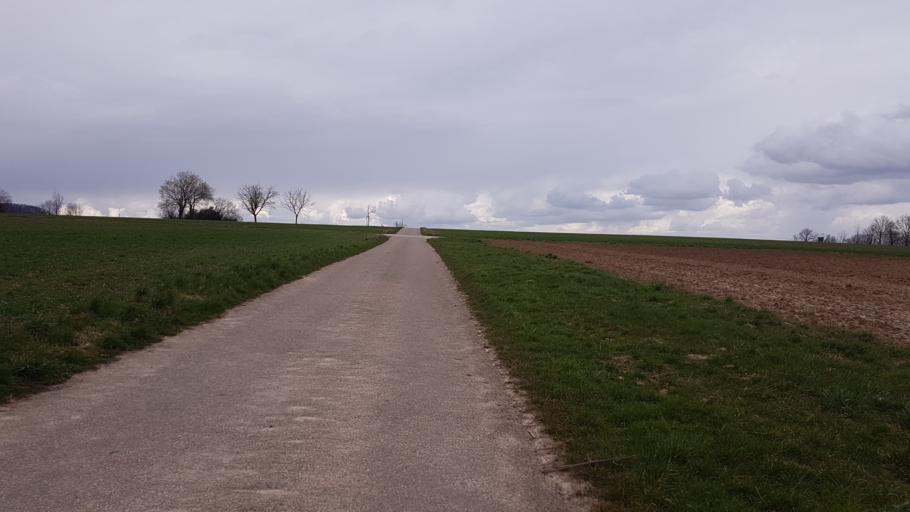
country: DE
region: Baden-Wuerttemberg
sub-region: Regierungsbezirk Stuttgart
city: Brackenheim
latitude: 49.0889
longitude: 9.0953
